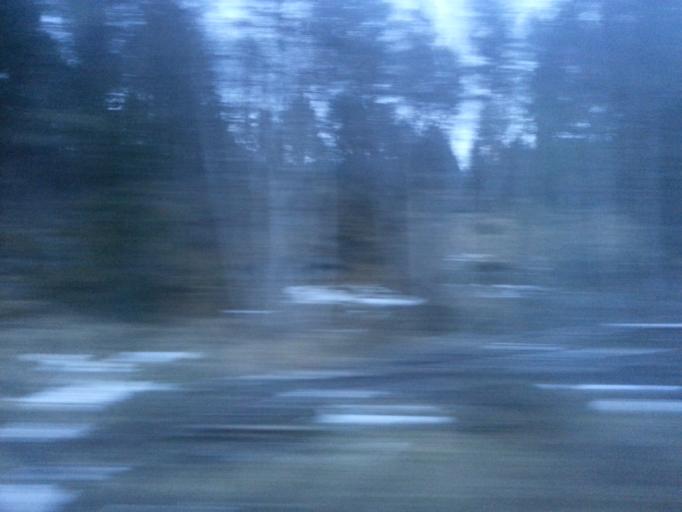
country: NO
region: Sor-Trondelag
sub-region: Rennebu
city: Berkak
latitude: 62.6993
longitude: 9.9519
